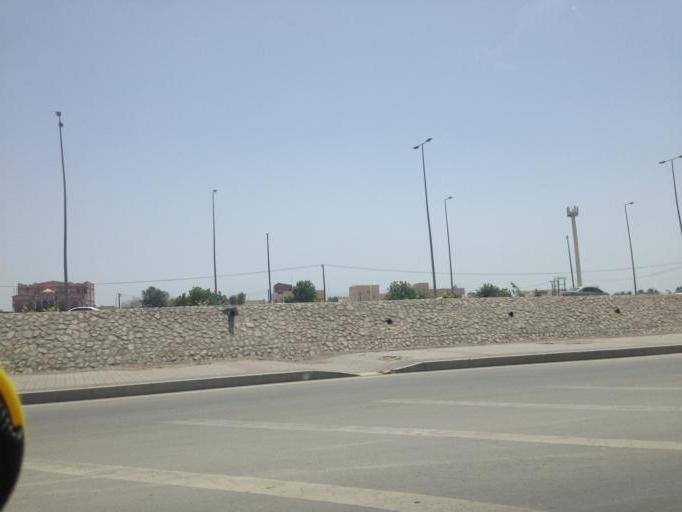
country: OM
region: Muhafazat Masqat
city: As Sib al Jadidah
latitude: 23.6771
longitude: 58.1331
